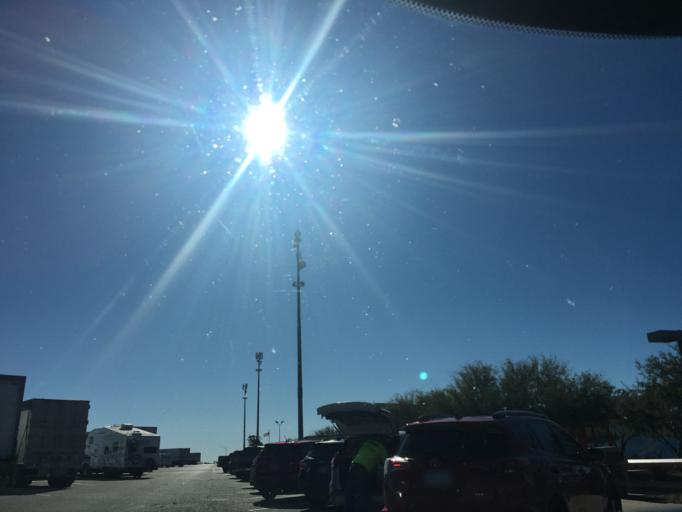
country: US
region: Arizona
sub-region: Yavapai County
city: Black Canyon City
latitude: 34.1870
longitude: -112.1342
